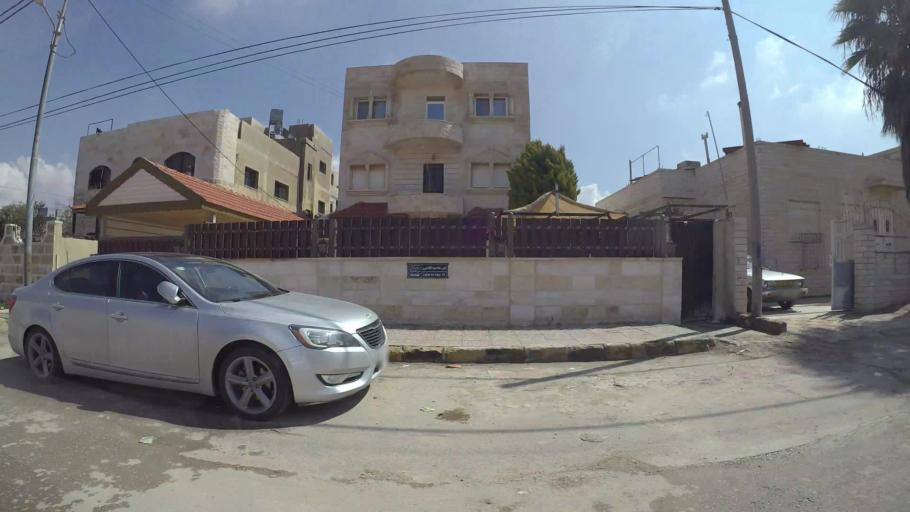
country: JO
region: Amman
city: Al Bunayyat ash Shamaliyah
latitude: 31.8981
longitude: 35.8932
